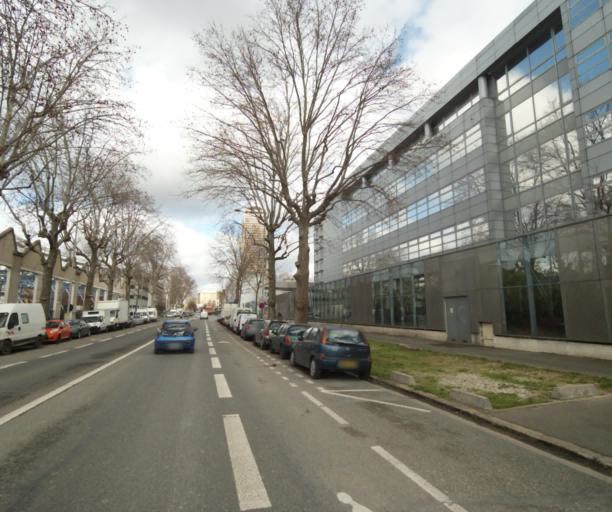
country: FR
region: Ile-de-France
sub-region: Paris
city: Saint-Ouen
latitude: 48.9161
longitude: 2.3443
